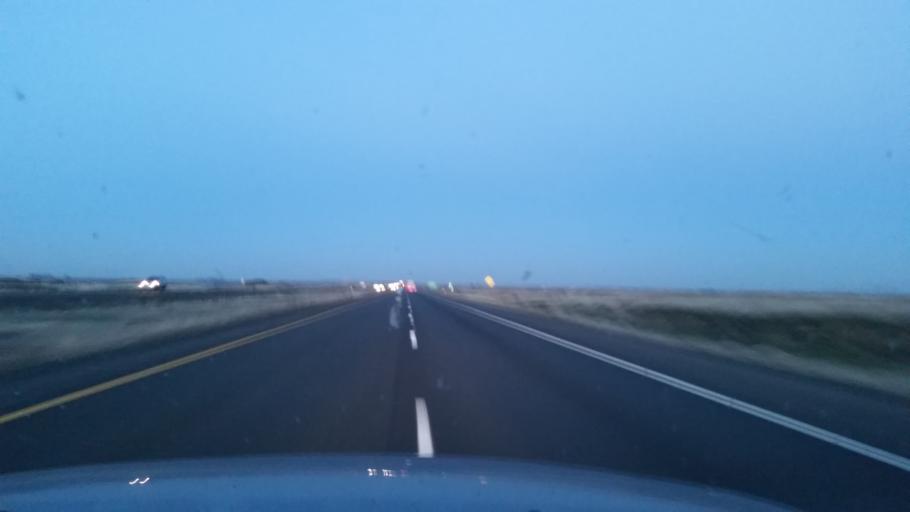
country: US
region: Washington
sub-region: Adams County
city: Ritzville
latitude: 47.1463
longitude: -118.3229
